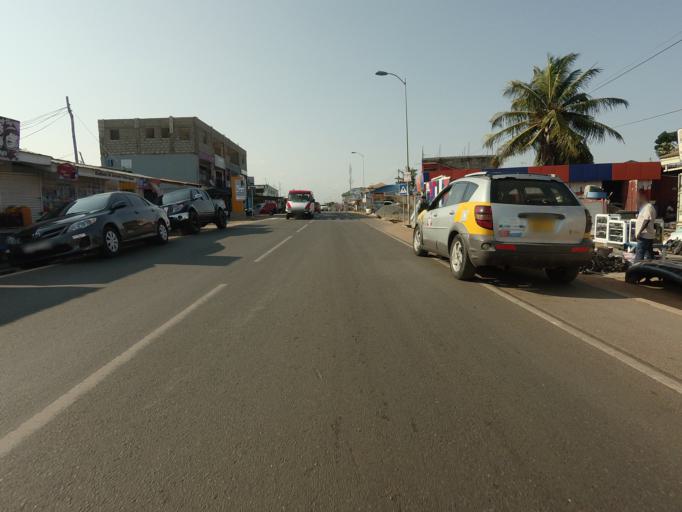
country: GH
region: Greater Accra
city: Nungua
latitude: 5.6304
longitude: -0.0763
